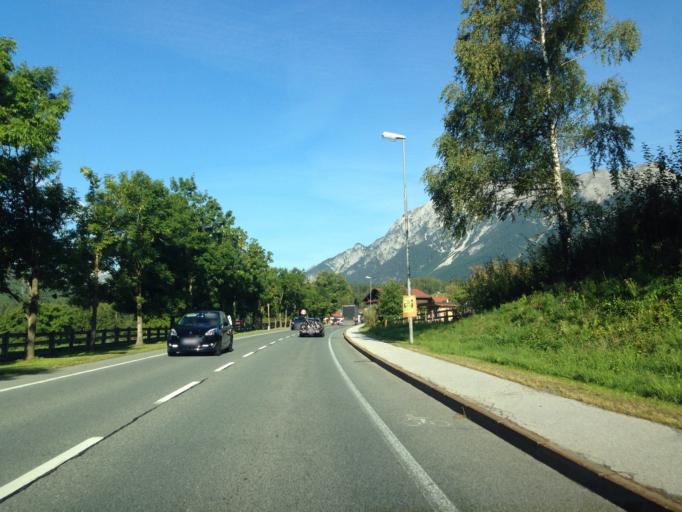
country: AT
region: Tyrol
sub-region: Politischer Bezirk Imst
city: Obsteig
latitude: 47.2985
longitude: 10.9249
